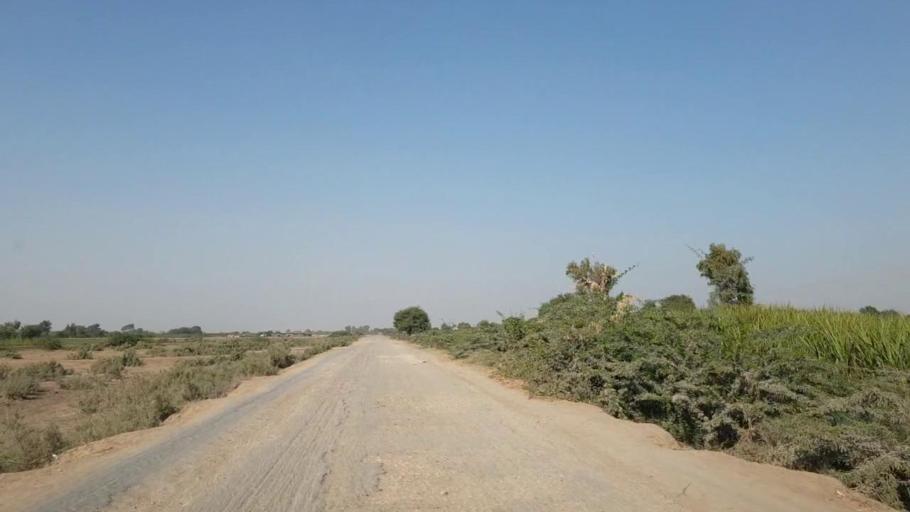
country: PK
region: Sindh
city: Digri
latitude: 25.0397
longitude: 69.1047
